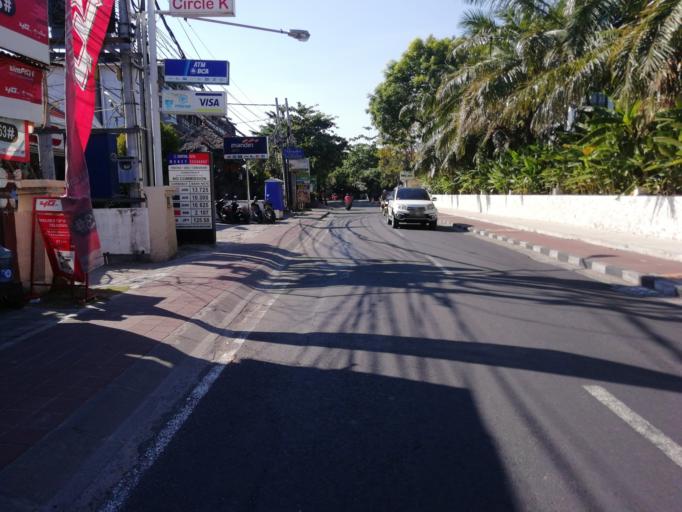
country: ID
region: Bali
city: Bualu
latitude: -8.7831
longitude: 115.2249
